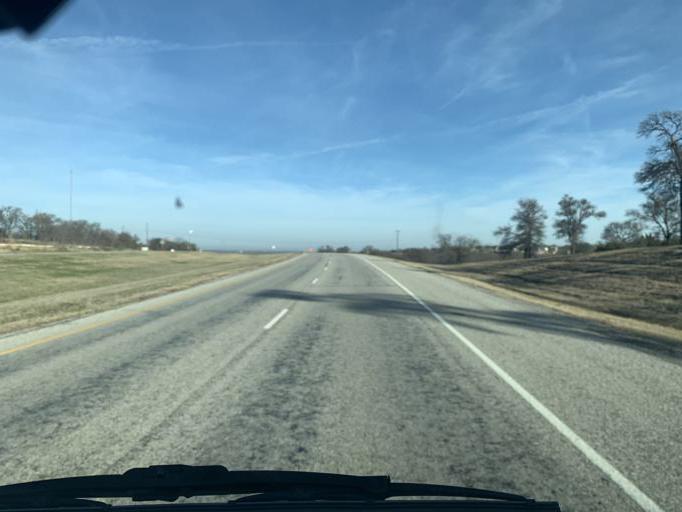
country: US
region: Texas
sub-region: Dallas County
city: Cedar Hill
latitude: 32.6382
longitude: -96.9720
